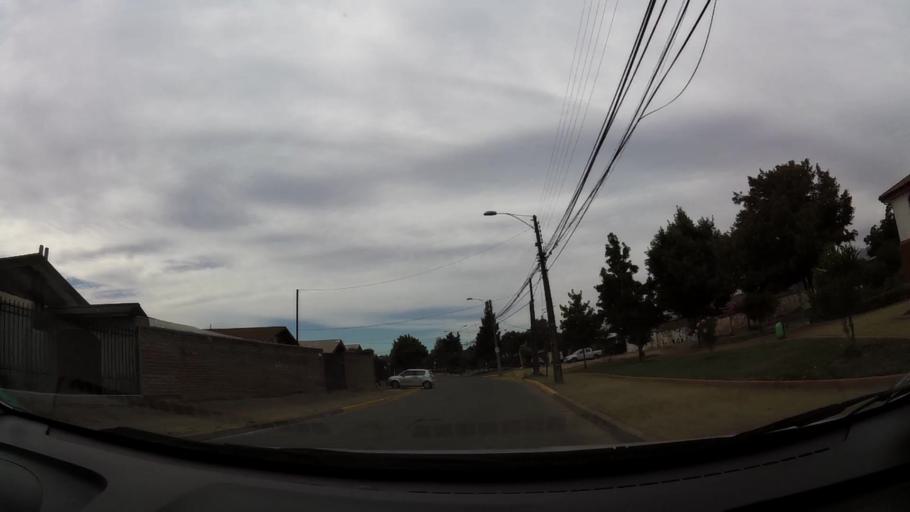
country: CL
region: O'Higgins
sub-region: Provincia de Cachapoal
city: Rancagua
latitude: -34.1487
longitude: -70.7392
